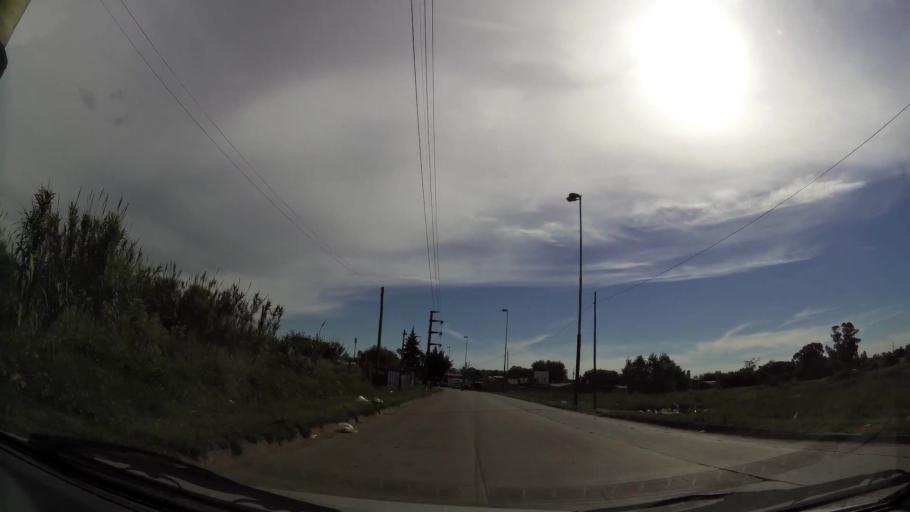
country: AR
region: Buenos Aires
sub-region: Partido de Almirante Brown
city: Adrogue
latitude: -34.8135
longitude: -58.3522
